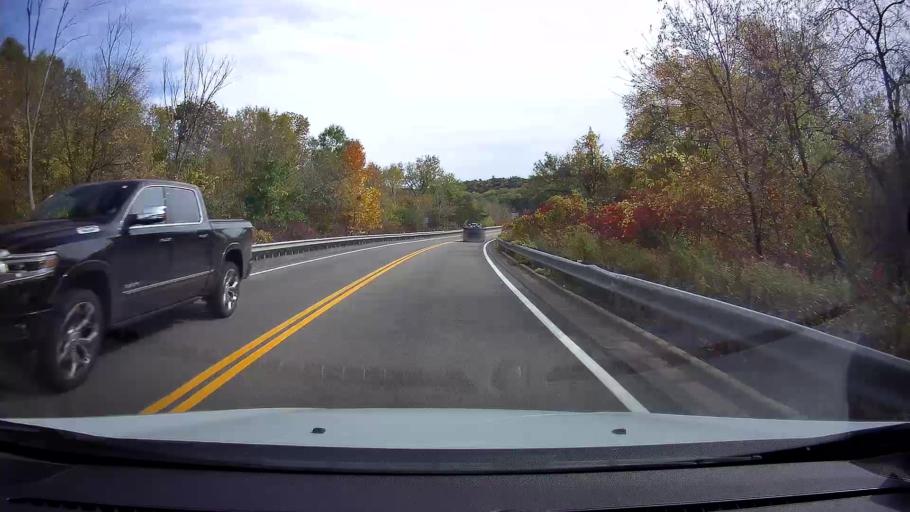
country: US
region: Wisconsin
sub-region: Polk County
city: Osceola
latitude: 45.3230
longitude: -92.7174
